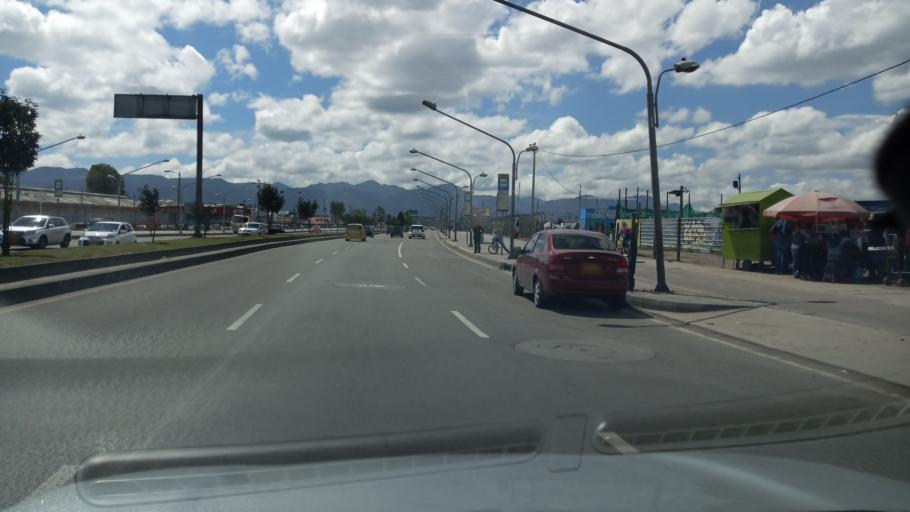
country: CO
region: Bogota D.C.
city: Bogota
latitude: 4.6917
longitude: -74.1203
